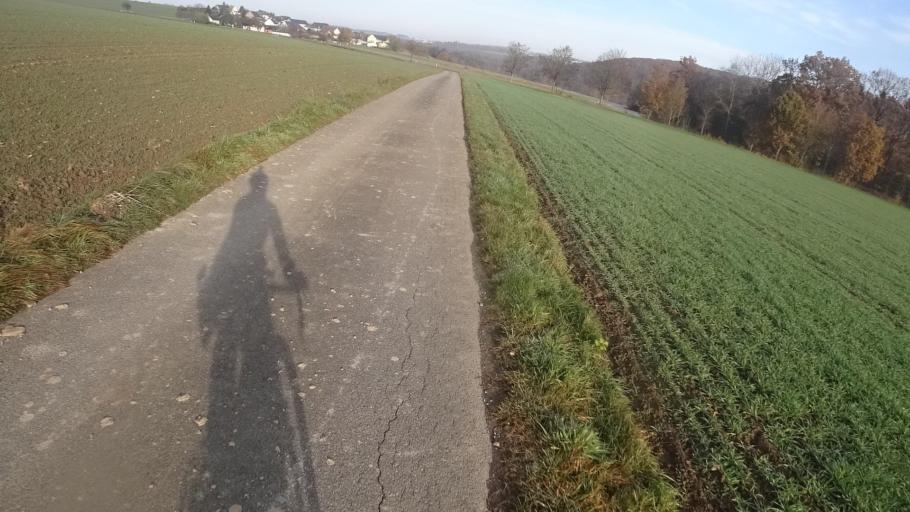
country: DE
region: Rheinland-Pfalz
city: Muhlpfad
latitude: 50.1173
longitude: 7.5596
